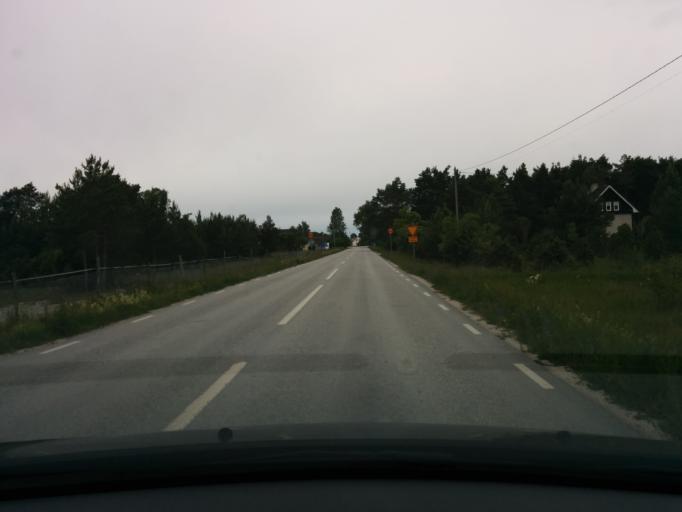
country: SE
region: Gotland
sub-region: Gotland
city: Slite
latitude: 57.6783
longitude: 18.7682
